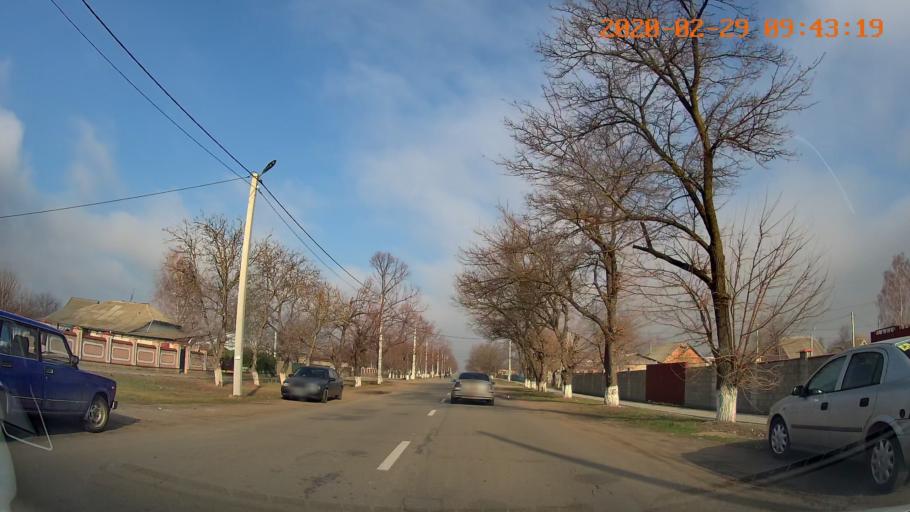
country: MD
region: Telenesti
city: Crasnoe
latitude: 46.6435
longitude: 29.8223
